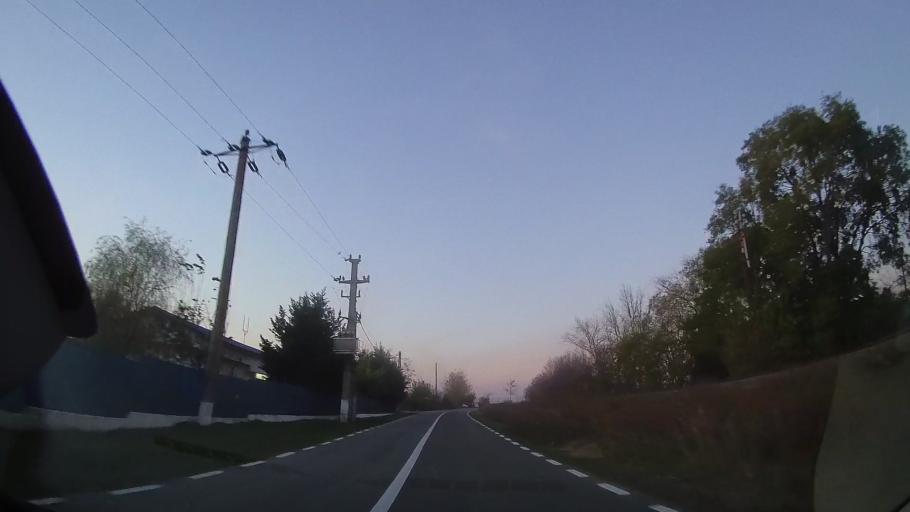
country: RO
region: Constanta
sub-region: Comuna Cobadin
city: Cobadin
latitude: 44.0520
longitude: 28.2477
